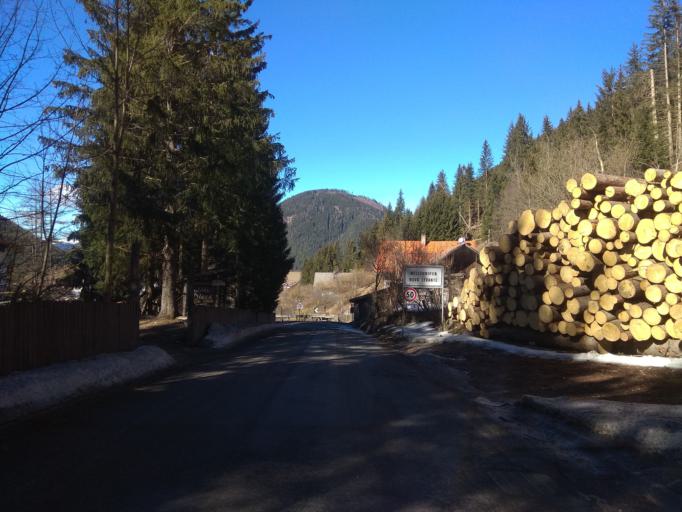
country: IT
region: Trentino-Alto Adige
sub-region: Bolzano
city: Nova Levante
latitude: 46.4207
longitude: 11.5611
